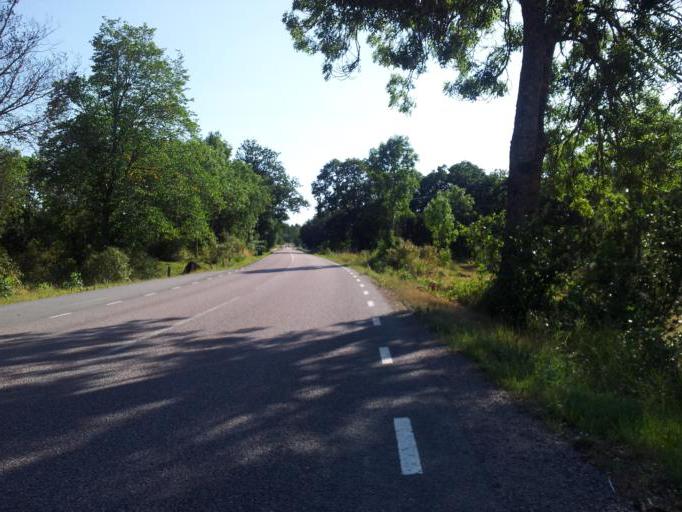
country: SE
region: Uppsala
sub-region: Knivsta Kommun
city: Knivsta
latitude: 59.8833
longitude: 17.9730
